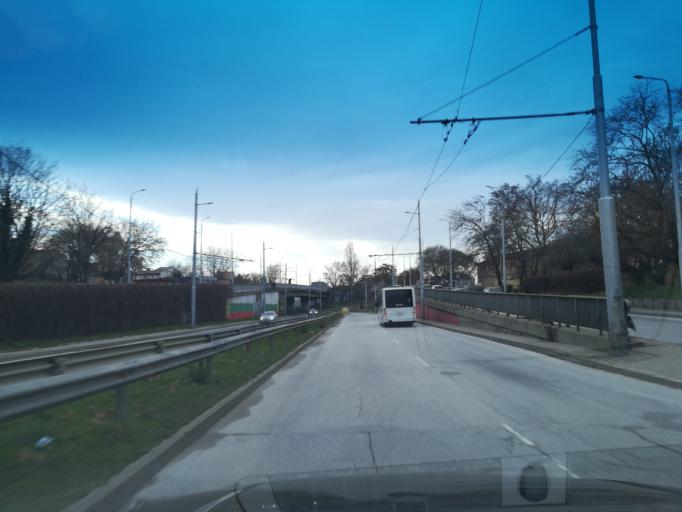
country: BG
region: Plovdiv
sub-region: Obshtina Plovdiv
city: Plovdiv
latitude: 42.1329
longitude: 24.7272
